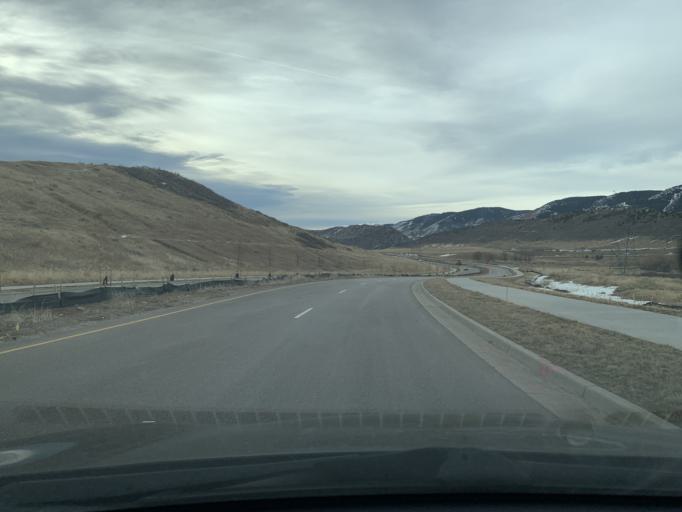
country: US
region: Colorado
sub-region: Jefferson County
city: West Pleasant View
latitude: 39.6820
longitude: -105.1830
